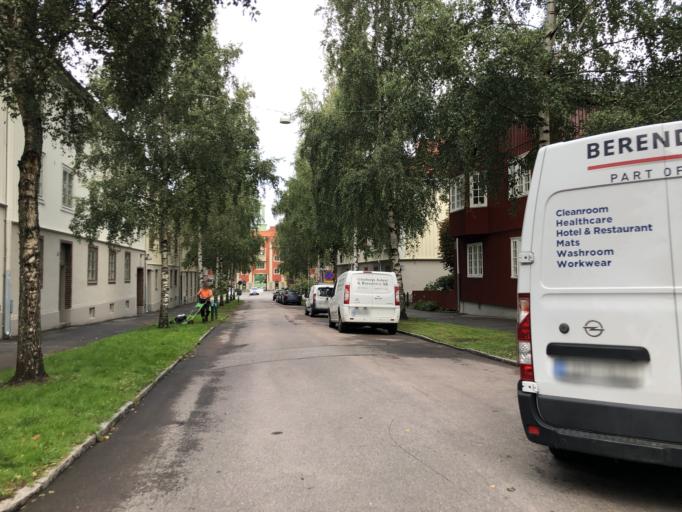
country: SE
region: Vaestra Goetaland
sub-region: Goteborg
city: Majorna
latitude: 57.6927
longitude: 11.9286
